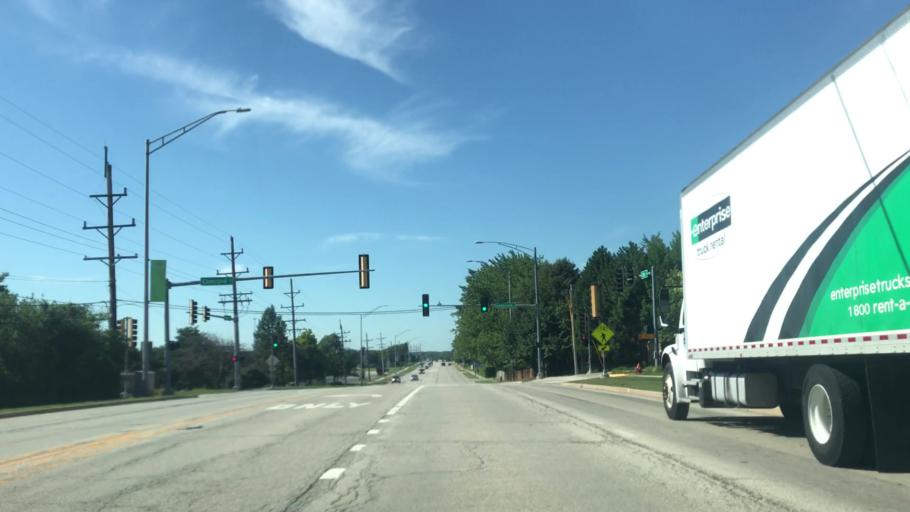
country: US
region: Illinois
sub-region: DuPage County
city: Darien
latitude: 41.7441
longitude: -87.9737
